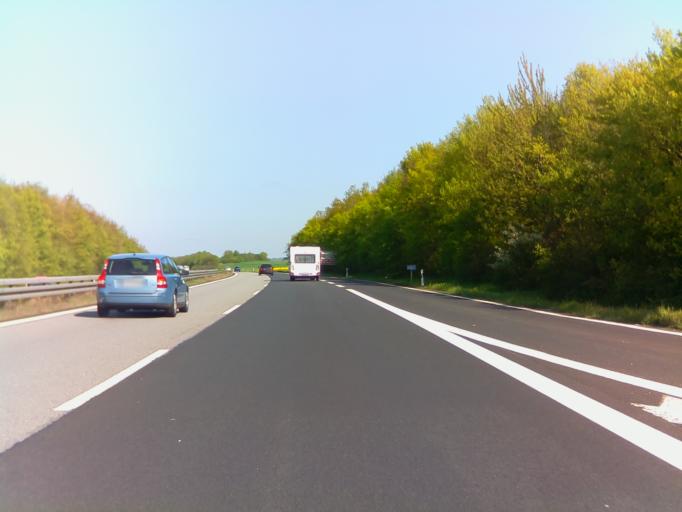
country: DE
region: Bavaria
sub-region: Regierungsbezirk Unterfranken
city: Kurnach
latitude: 49.8313
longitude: 10.0391
